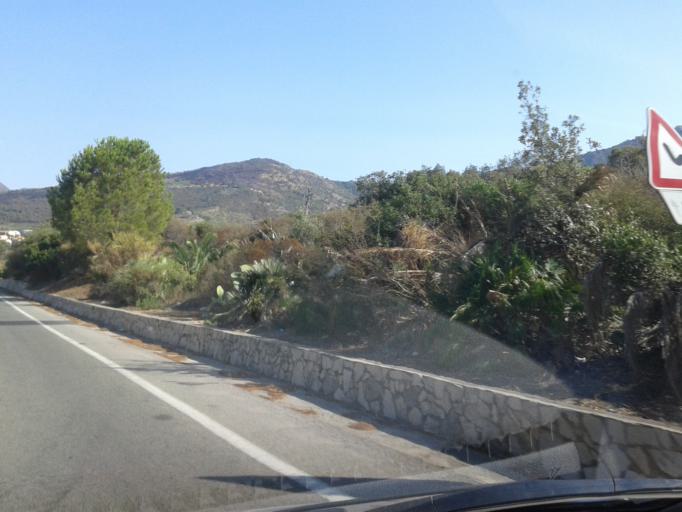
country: IT
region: Sicily
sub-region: Palermo
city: Finale
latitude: 38.0245
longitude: 14.1486
